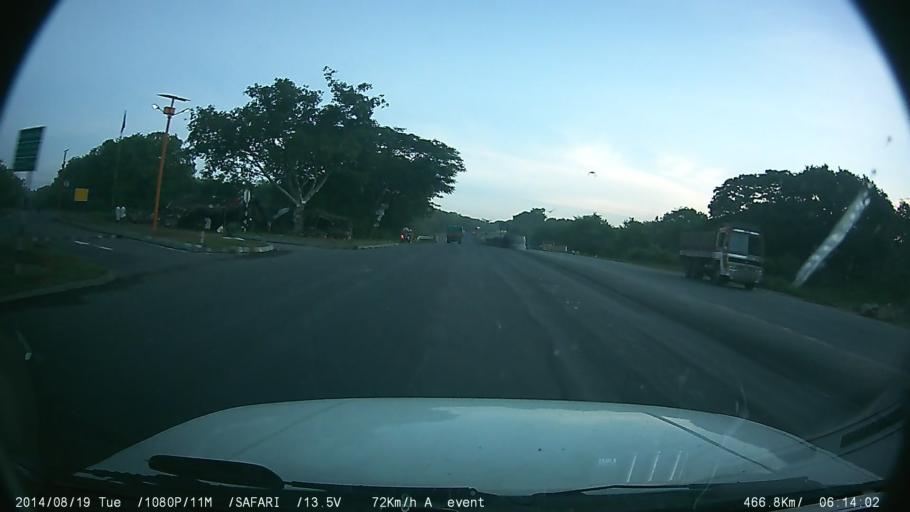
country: IN
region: Tamil Nadu
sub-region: Dharmapuri
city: Dharmapuri
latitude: 11.9695
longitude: 78.0512
